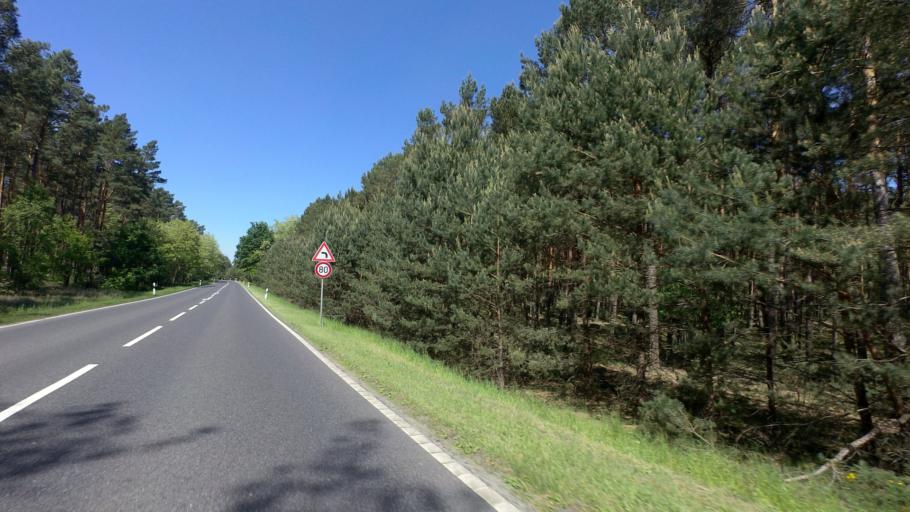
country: DE
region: Brandenburg
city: Lieberose
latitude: 51.9532
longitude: 14.3315
